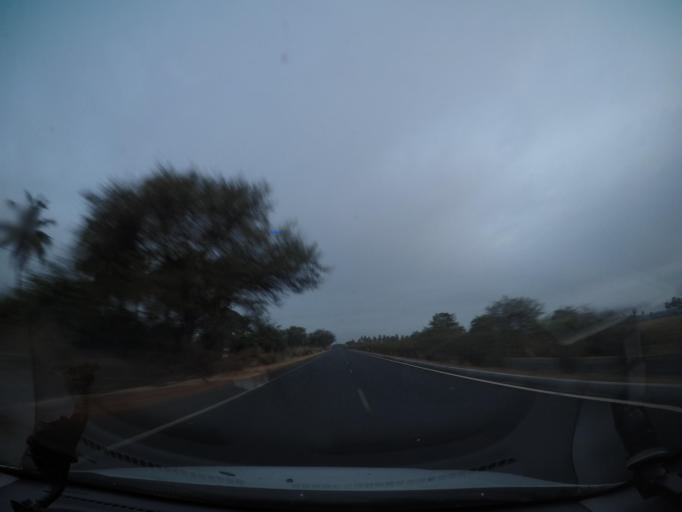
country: IN
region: Andhra Pradesh
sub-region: West Godavari
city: Tadepallegudem
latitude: 16.8098
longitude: 81.3535
